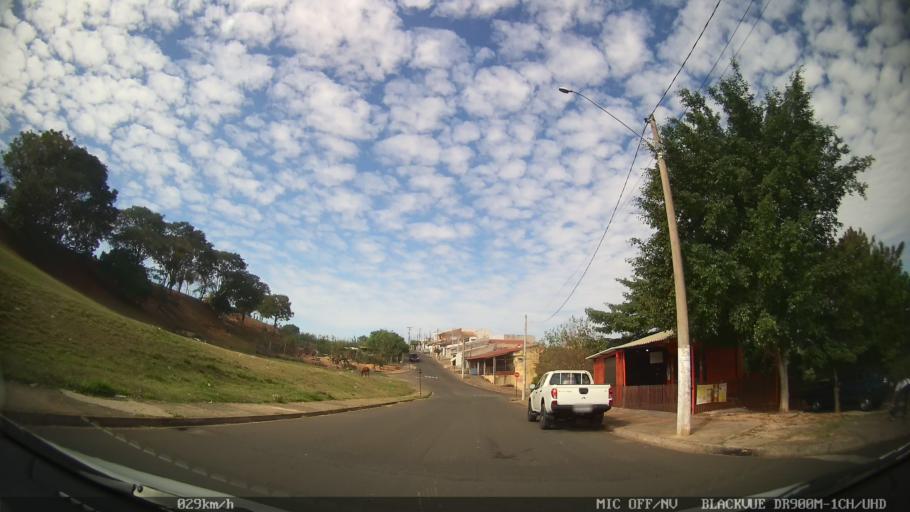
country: BR
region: Sao Paulo
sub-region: Santa Barbara D'Oeste
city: Santa Barbara d'Oeste
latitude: -22.7728
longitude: -47.3941
